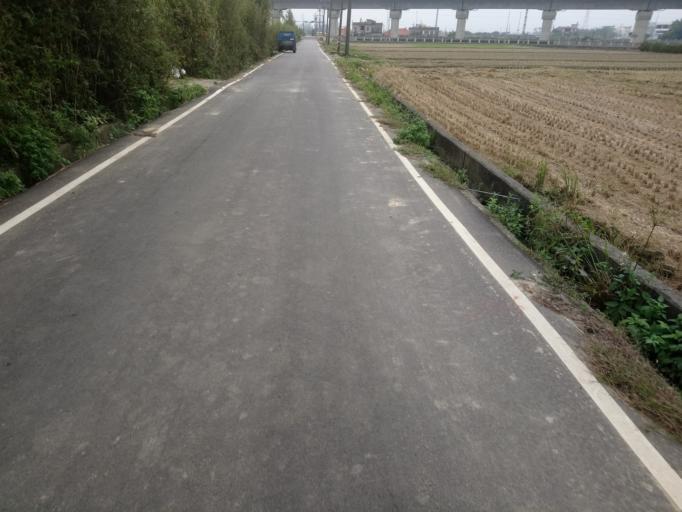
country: TW
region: Taiwan
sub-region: Hsinchu
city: Zhubei
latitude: 24.8880
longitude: 121.0757
